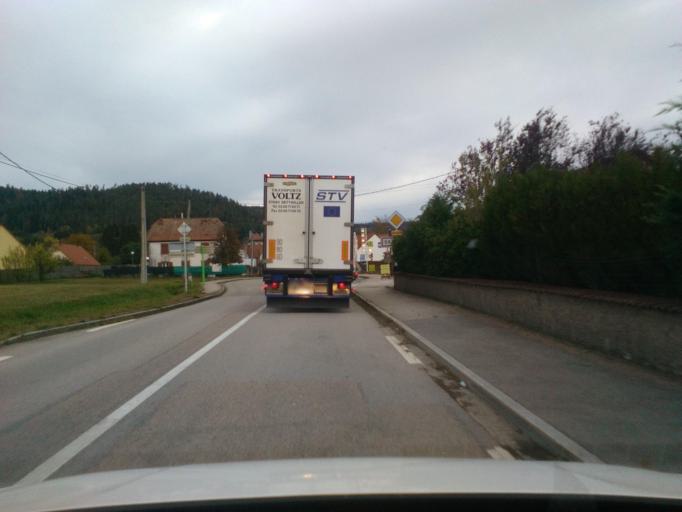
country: FR
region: Lorraine
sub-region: Departement des Vosges
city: Ban-de-Laveline
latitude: 48.3439
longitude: 7.1077
